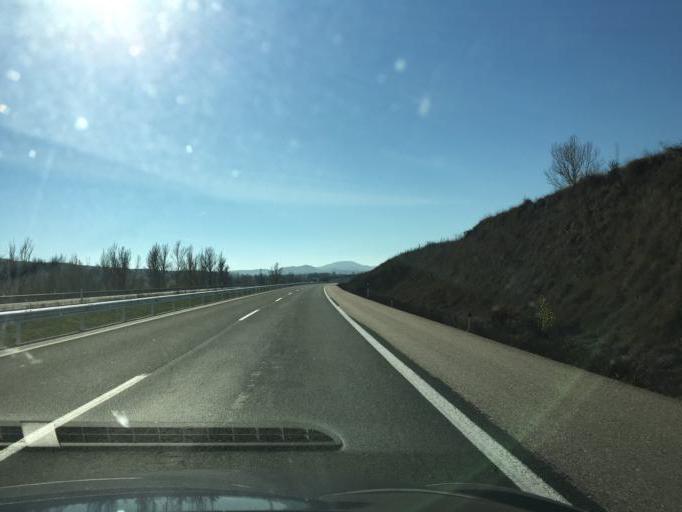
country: ES
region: Castille and Leon
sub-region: Provincia de Burgos
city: Pradanos de Bureba
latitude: 42.5076
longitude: -3.3484
